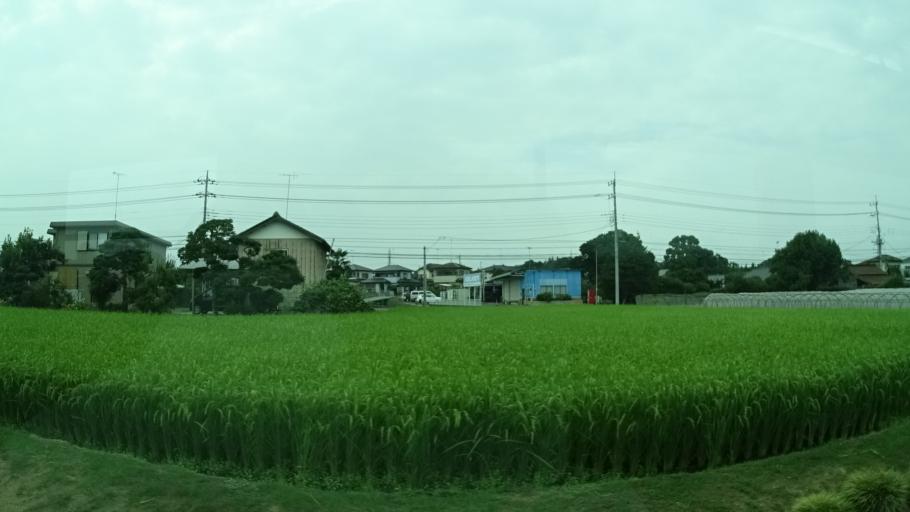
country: JP
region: Tochigi
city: Mooka
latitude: 36.4161
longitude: 139.9833
